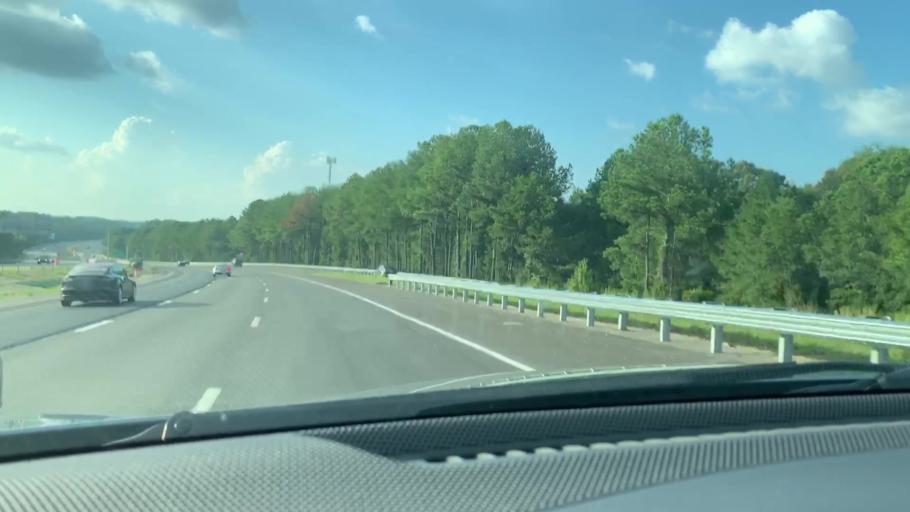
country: US
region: South Carolina
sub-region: Richland County
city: Woodfield
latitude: 34.0705
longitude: -80.9239
